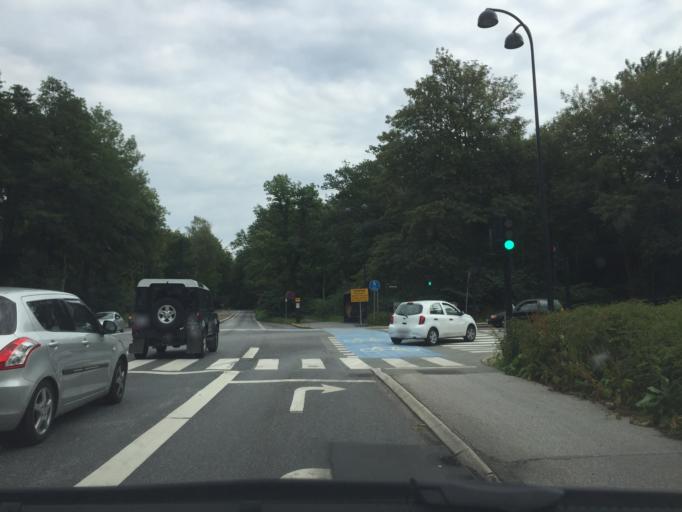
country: DK
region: Capital Region
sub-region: Gentofte Kommune
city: Charlottenlund
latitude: 55.7692
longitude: 12.5601
